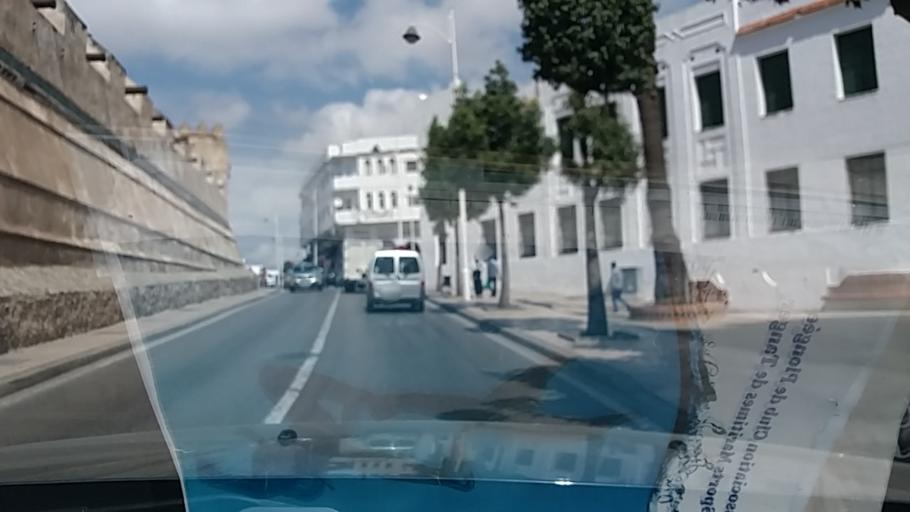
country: MA
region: Tanger-Tetouan
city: Tetouan
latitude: 35.5699
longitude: -5.3635
